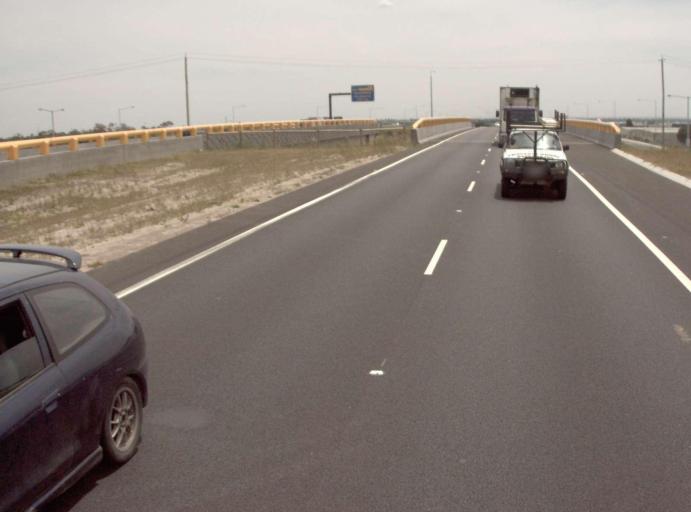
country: AU
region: Victoria
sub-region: Frankston
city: Carrum Downs
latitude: -38.1098
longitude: 145.1625
